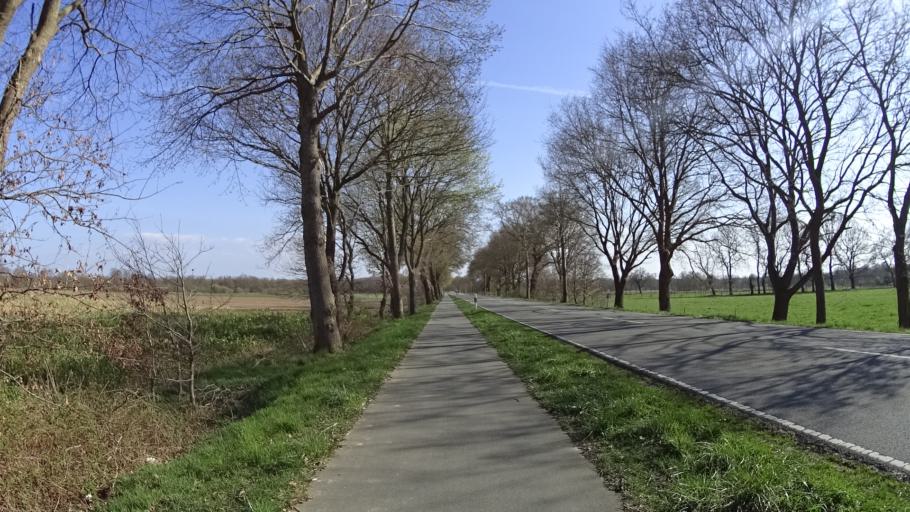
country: DE
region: Lower Saxony
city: Dorpen
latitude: 52.9752
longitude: 7.3105
